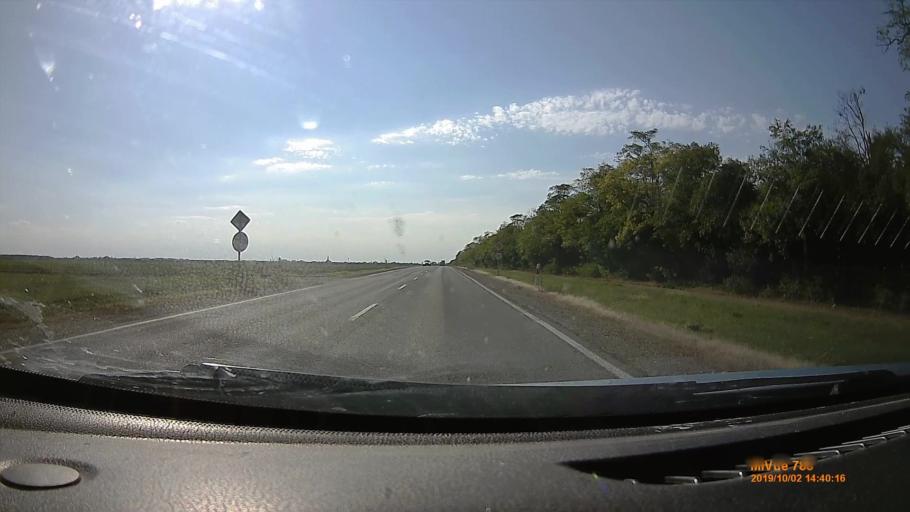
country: HU
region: Heves
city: Szihalom
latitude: 47.7880
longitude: 20.5079
